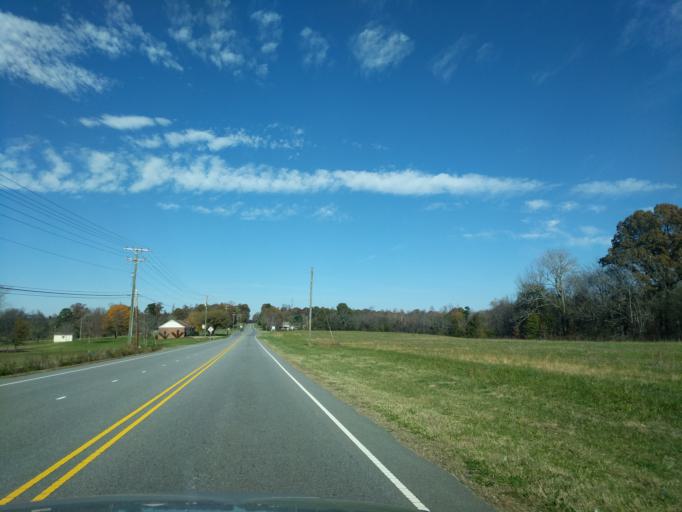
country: US
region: North Carolina
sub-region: Catawba County
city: Maiden
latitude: 35.5958
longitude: -81.2555
